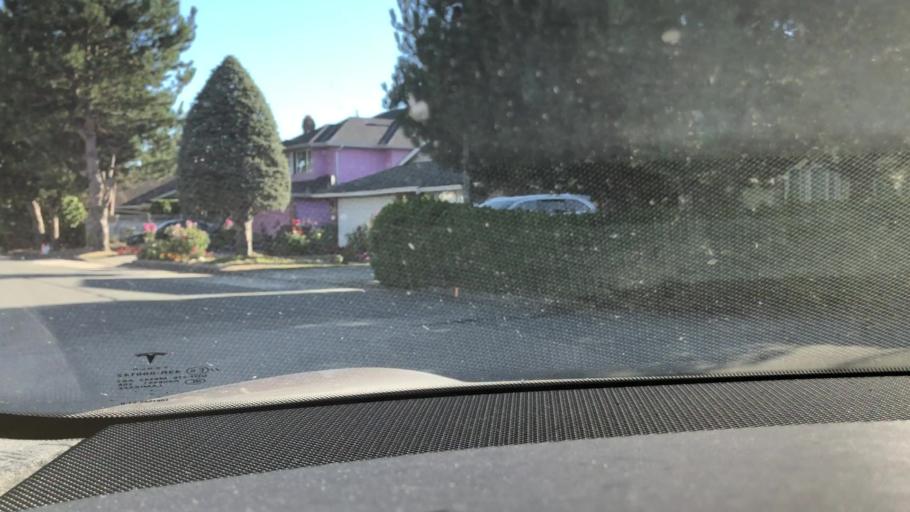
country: CA
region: British Columbia
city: Richmond
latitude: 49.1468
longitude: -123.1603
